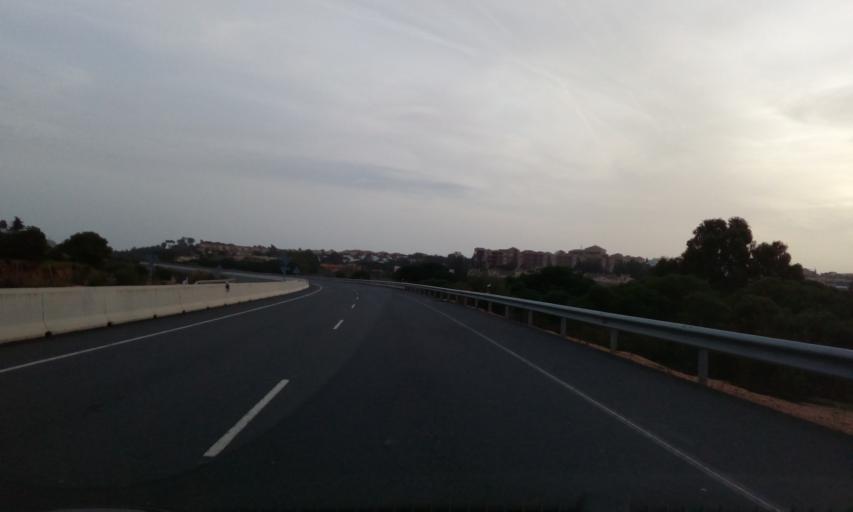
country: ES
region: Andalusia
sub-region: Provincia de Huelva
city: Lepe
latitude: 37.2205
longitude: -7.2214
